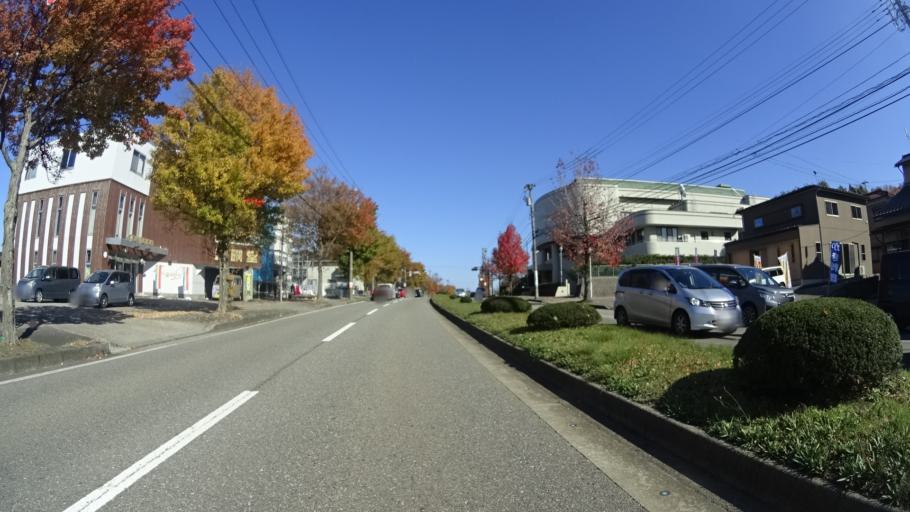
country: JP
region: Ishikawa
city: Nonoichi
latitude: 36.5154
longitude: 136.6313
